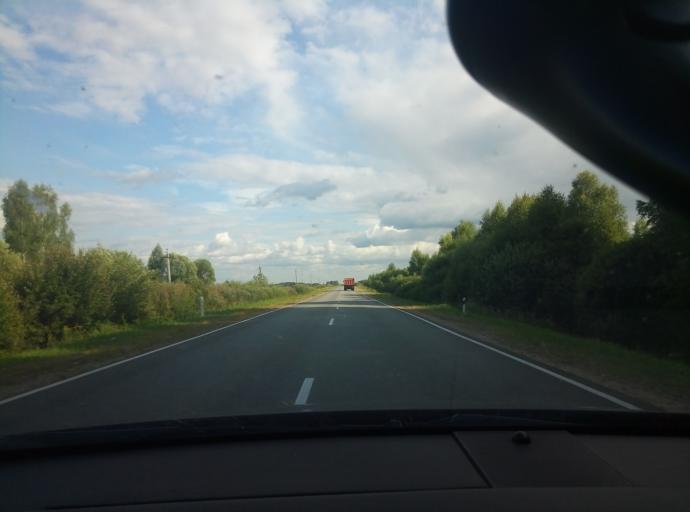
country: RU
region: Kaluga
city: Yukhnov
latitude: 54.6262
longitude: 35.3450
